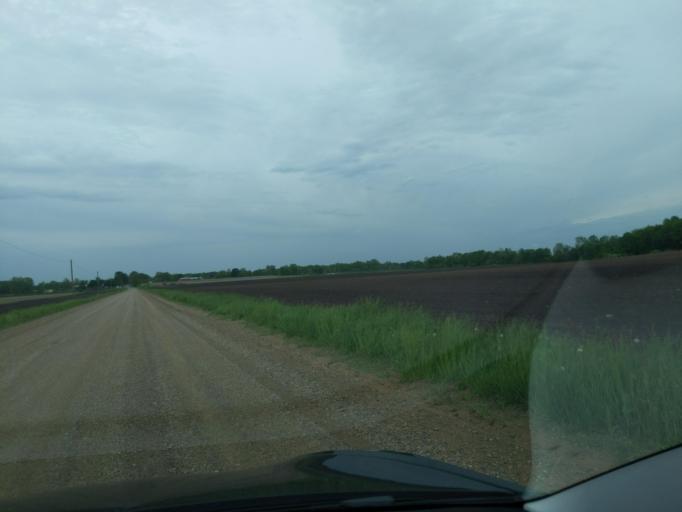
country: US
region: Michigan
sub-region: Ingham County
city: Stockbridge
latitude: 42.4221
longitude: -84.2142
